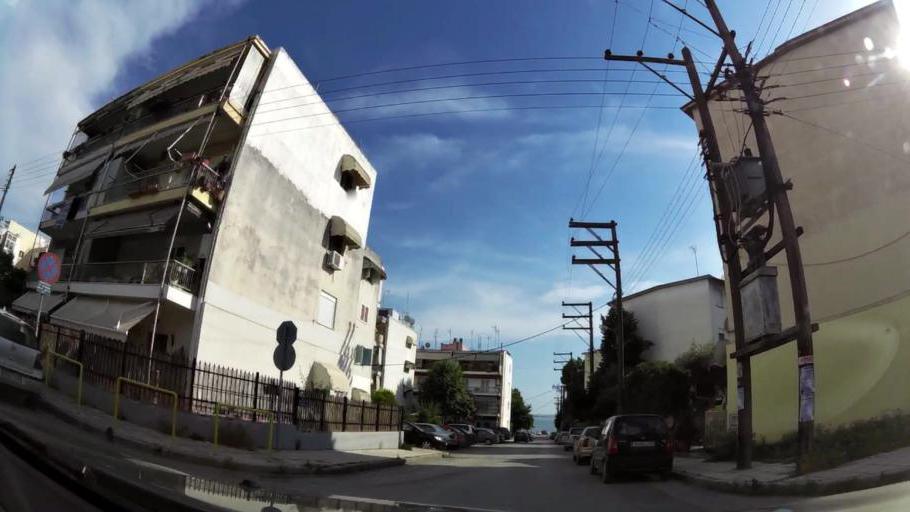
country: GR
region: Central Macedonia
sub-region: Nomos Thessalonikis
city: Kalamaria
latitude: 40.5662
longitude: 22.9620
